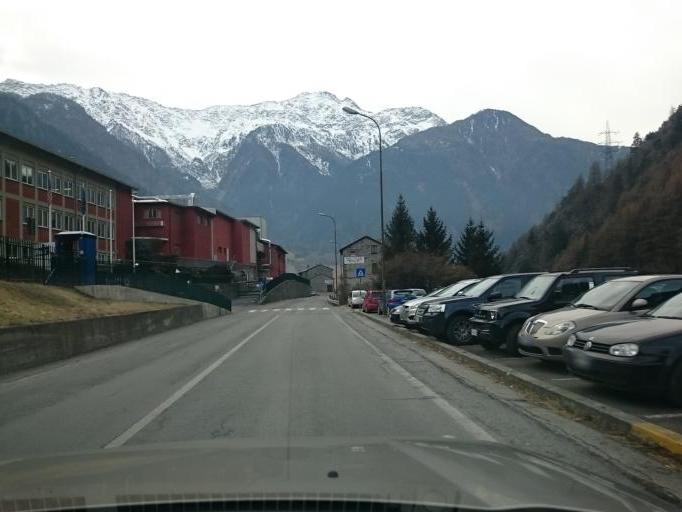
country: IT
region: Lombardy
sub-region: Provincia di Sondrio
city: Sondalo
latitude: 46.3369
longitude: 10.3496
